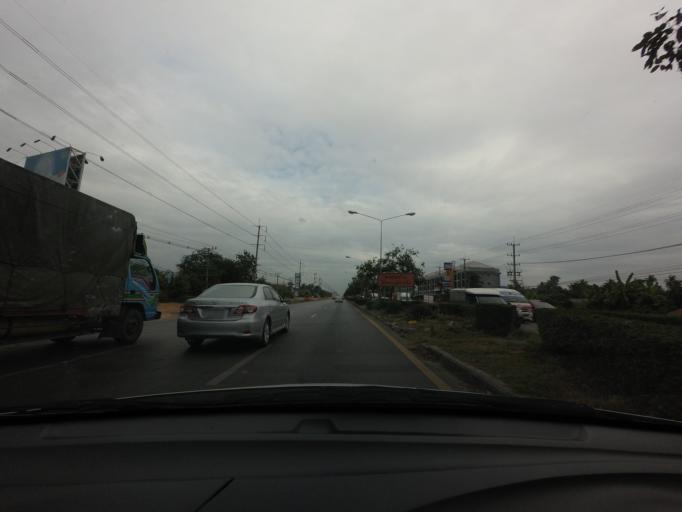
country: TH
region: Nakhon Pathom
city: Nakhon Chai Si
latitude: 13.7682
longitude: 100.1967
